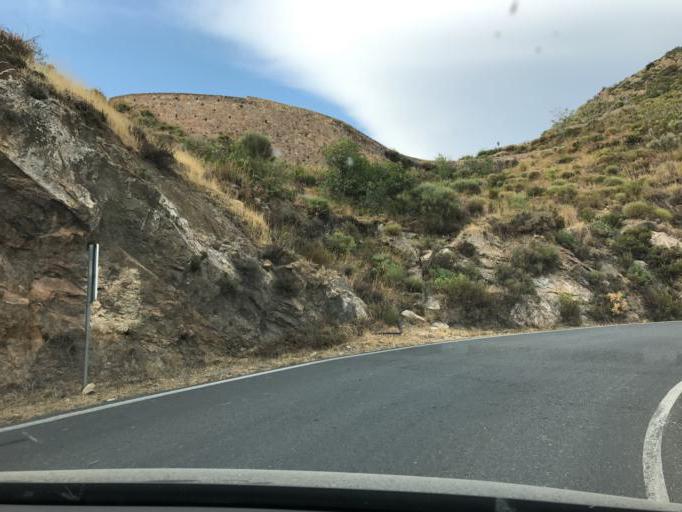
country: ES
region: Andalusia
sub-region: Provincia de Granada
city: Cadiar
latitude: 36.9609
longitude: -3.1765
